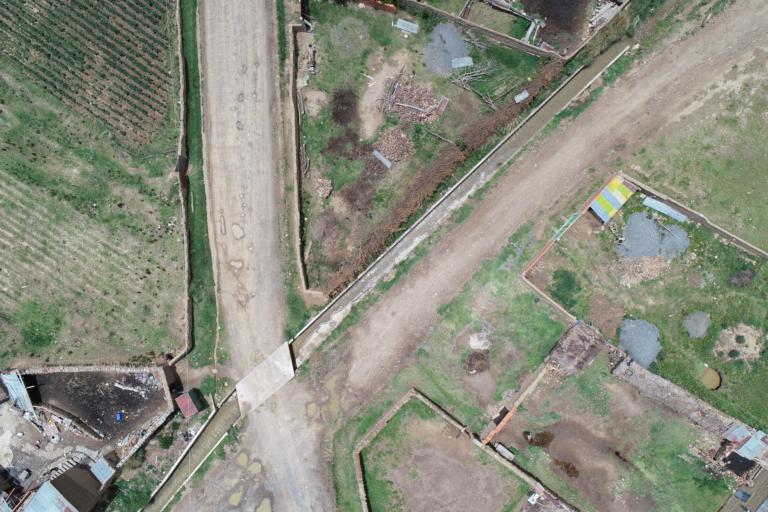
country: BO
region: La Paz
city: Huarina
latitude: -16.1886
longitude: -68.6038
